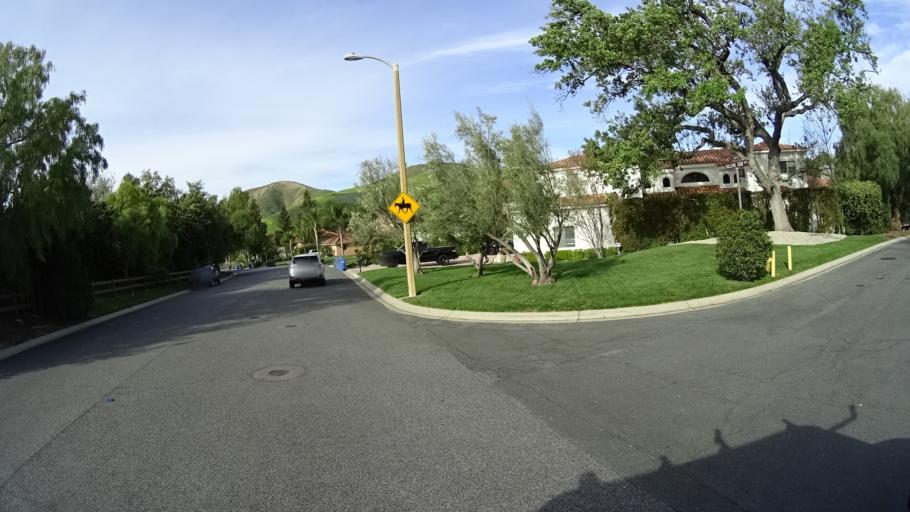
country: US
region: California
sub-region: Ventura County
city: Oak Park
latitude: 34.1872
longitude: -118.7870
